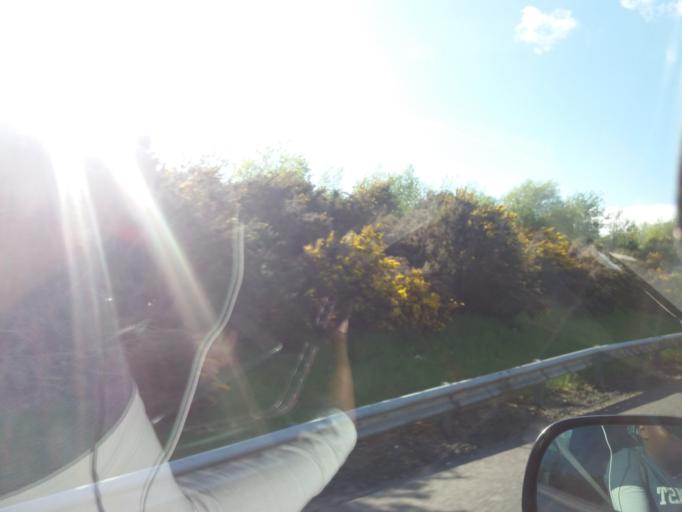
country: IE
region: Munster
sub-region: Waterford
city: Waterford
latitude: 52.3190
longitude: -7.1437
